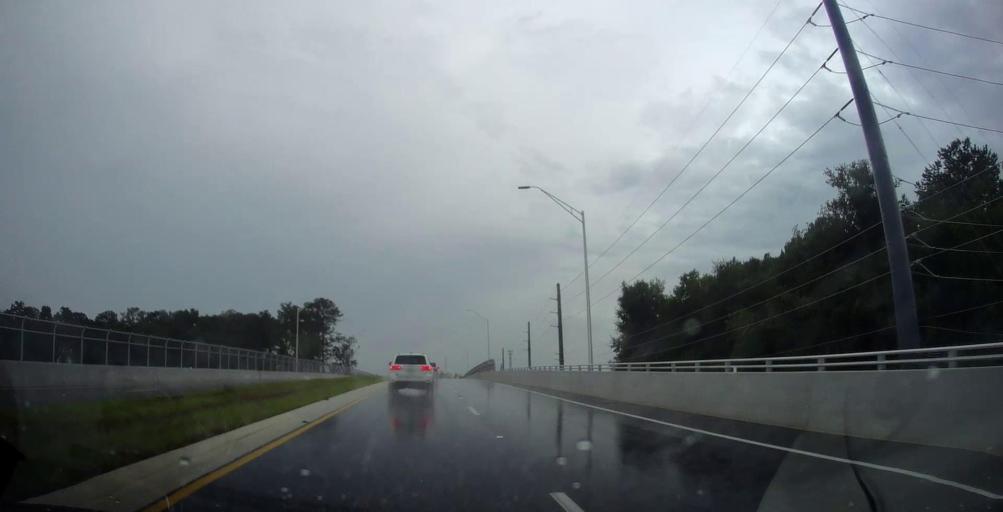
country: US
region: Florida
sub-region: Marion County
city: Ocala
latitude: 29.2119
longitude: -82.0870
